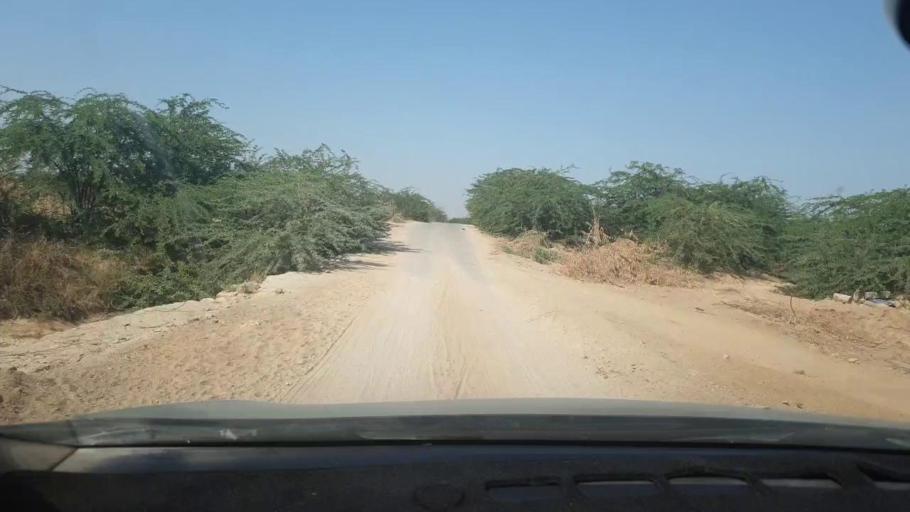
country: PK
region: Sindh
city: Malir Cantonment
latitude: 25.1592
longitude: 67.1642
